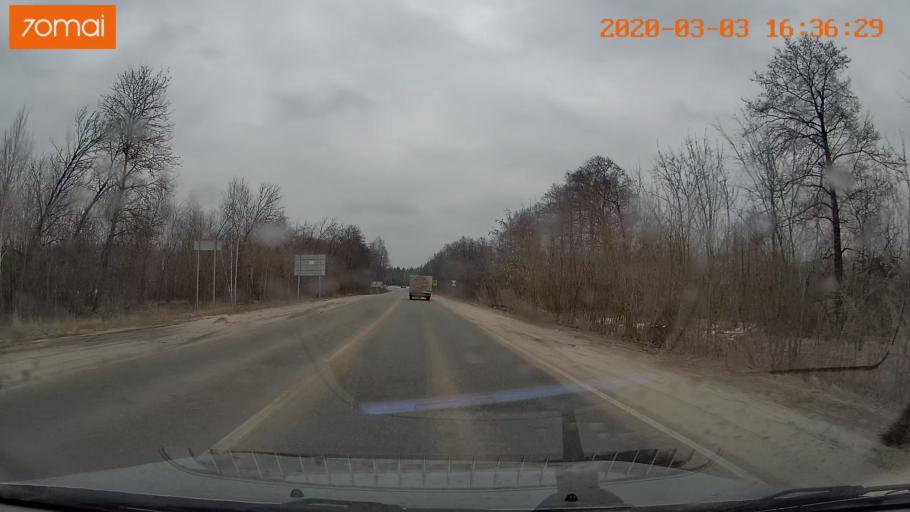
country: RU
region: Moskovskaya
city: Lopatinskiy
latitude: 55.3993
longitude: 38.7733
